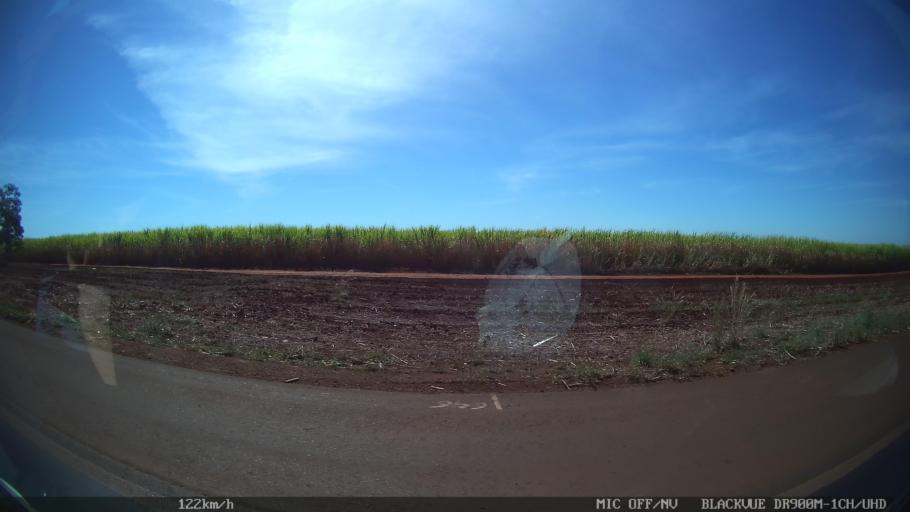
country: BR
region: Sao Paulo
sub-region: Ipua
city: Ipua
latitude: -20.4990
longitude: -47.9591
